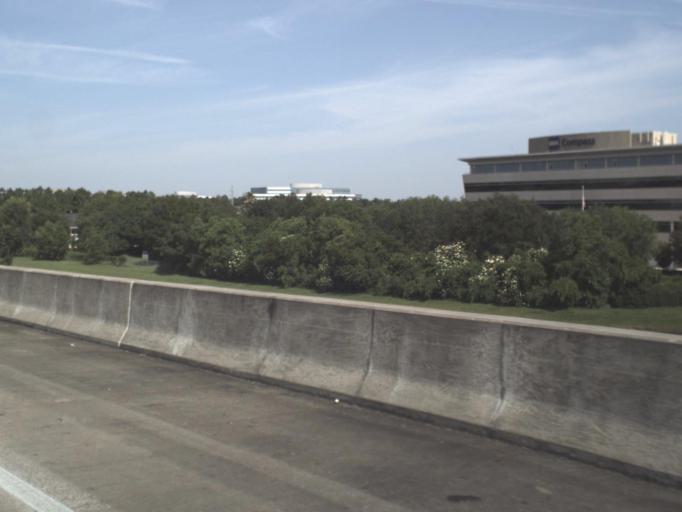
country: US
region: Florida
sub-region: Duval County
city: Jacksonville
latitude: 30.2503
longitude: -81.5360
